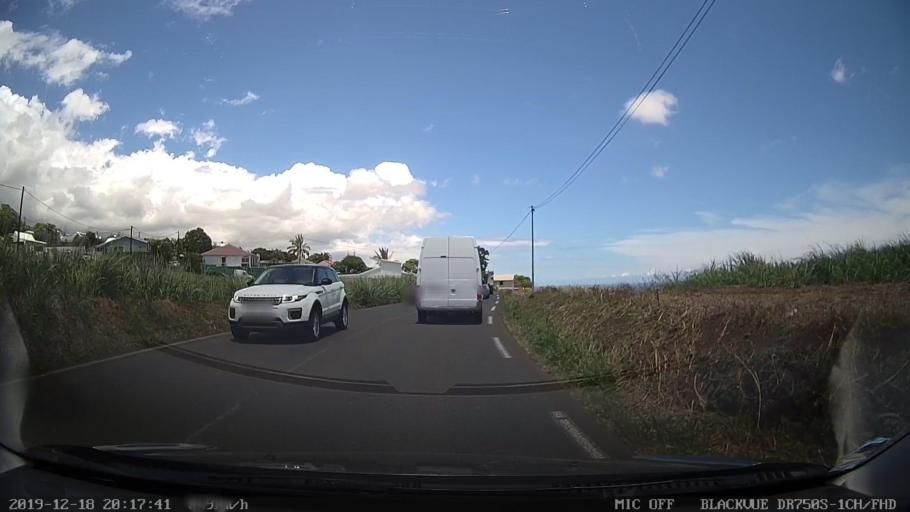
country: RE
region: Reunion
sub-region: Reunion
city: Sainte-Marie
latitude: -20.9210
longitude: 55.5392
